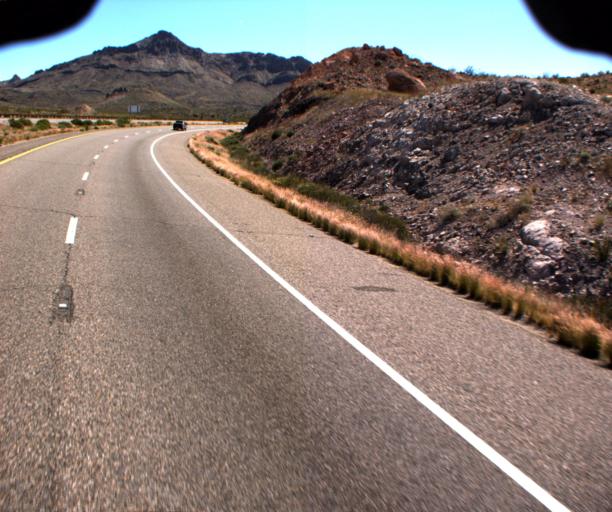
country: US
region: Nevada
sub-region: Clark County
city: Laughlin
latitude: 35.1993
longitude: -114.4247
